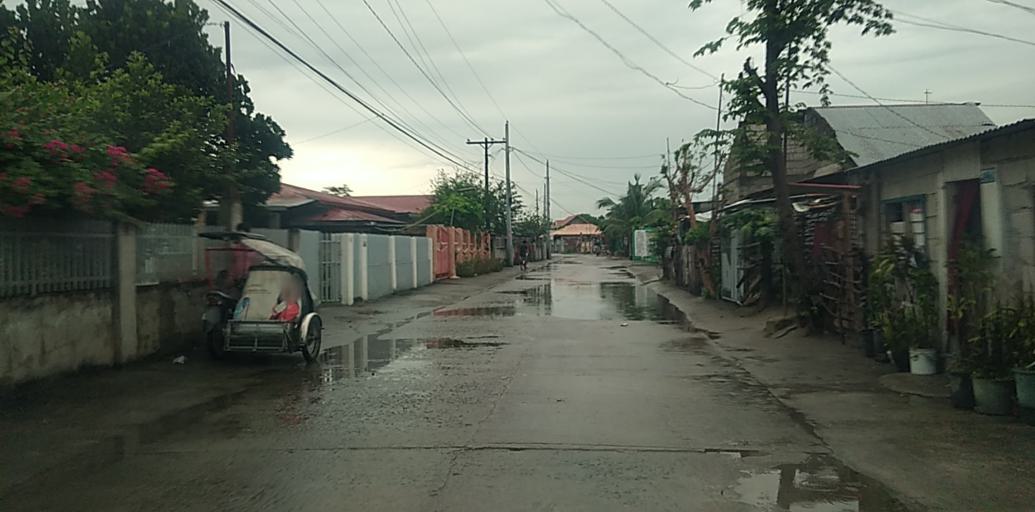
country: PH
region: Central Luzon
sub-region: Province of Pampanga
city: Arayat
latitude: 15.1397
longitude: 120.7365
